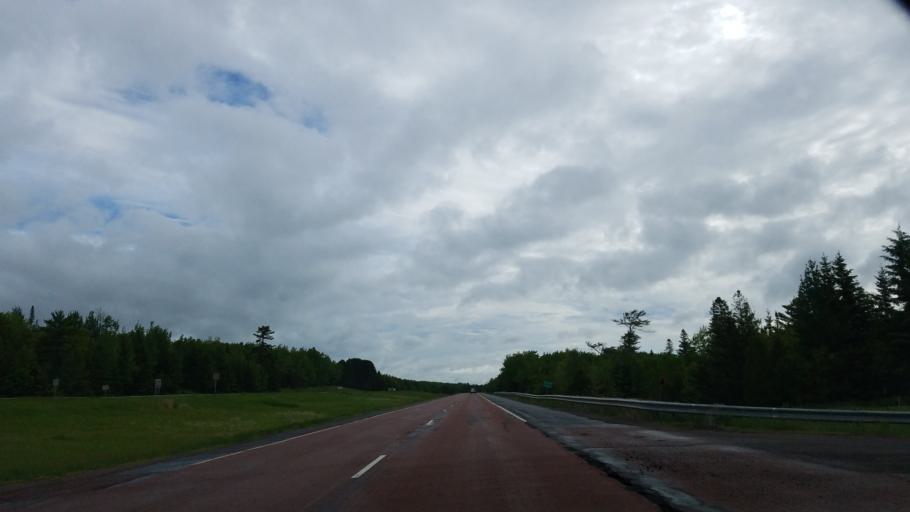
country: US
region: Minnesota
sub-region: Saint Louis County
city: Arnold
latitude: 46.9004
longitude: -91.9005
